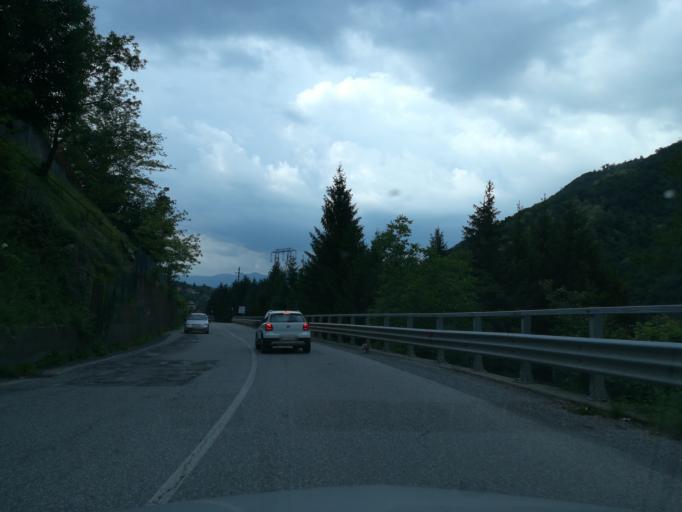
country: IT
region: Lombardy
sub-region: Provincia di Bergamo
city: Strozza
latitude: 45.7668
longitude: 9.5842
